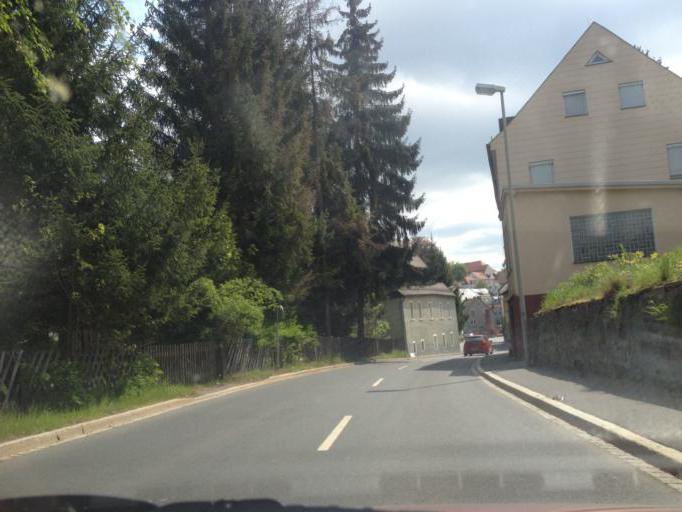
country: DE
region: Bavaria
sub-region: Upper Franconia
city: Arzberg
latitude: 50.0585
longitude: 12.1829
